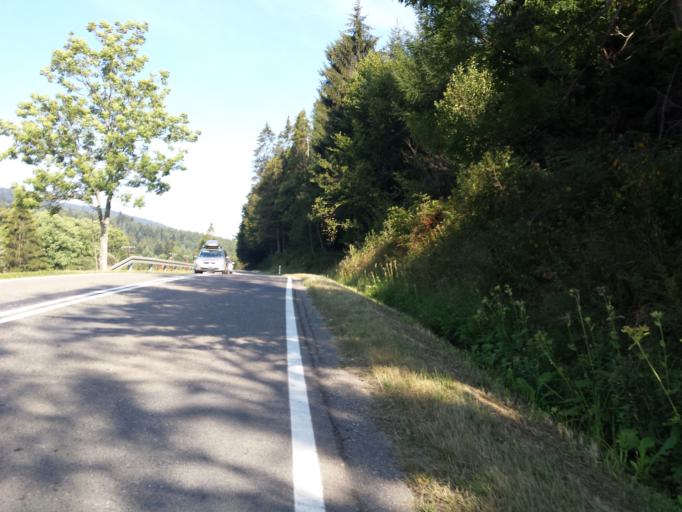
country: PL
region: Subcarpathian Voivodeship
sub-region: Powiat leski
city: Cisna
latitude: 49.2183
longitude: 22.3183
